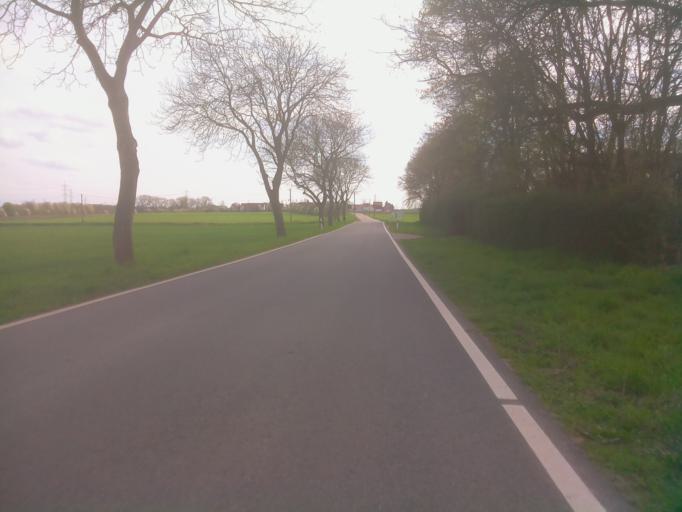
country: DE
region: Hesse
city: Viernheim
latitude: 49.5214
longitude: 8.5797
